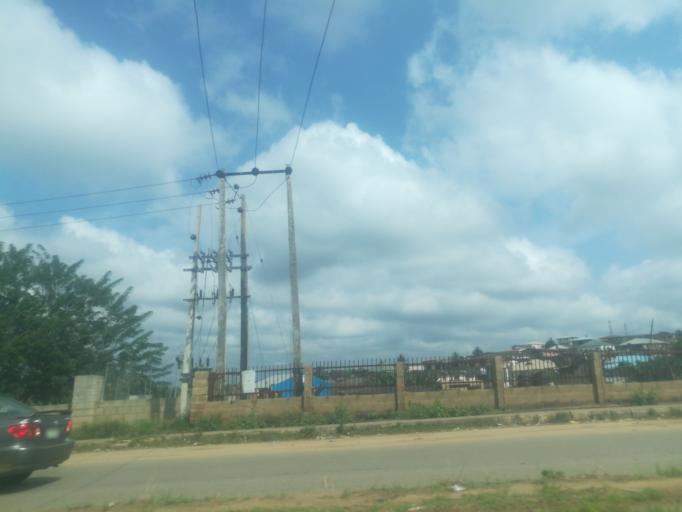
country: NG
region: Oyo
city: Ibadan
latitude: 7.3313
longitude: 3.8625
